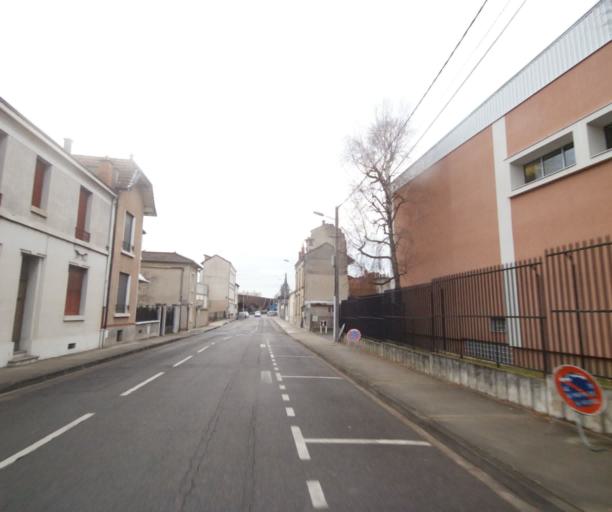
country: FR
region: Rhone-Alpes
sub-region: Departement de la Loire
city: Roanne
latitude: 46.0394
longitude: 4.0746
